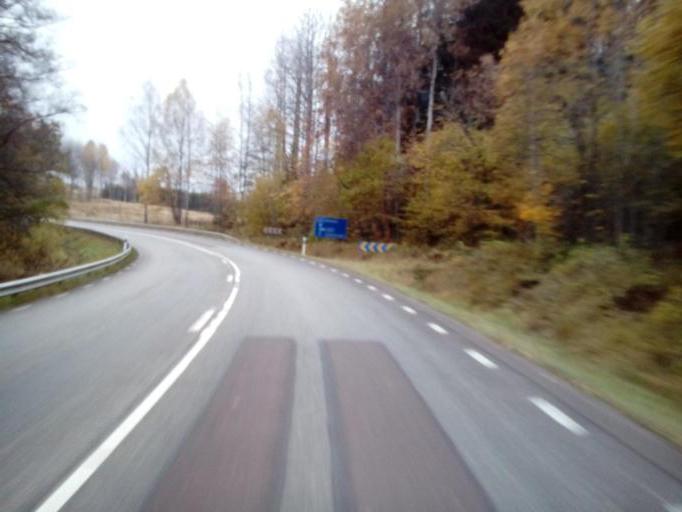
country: SE
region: OErebro
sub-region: Laxa Kommun
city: Laxa
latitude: 59.1127
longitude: 14.5396
